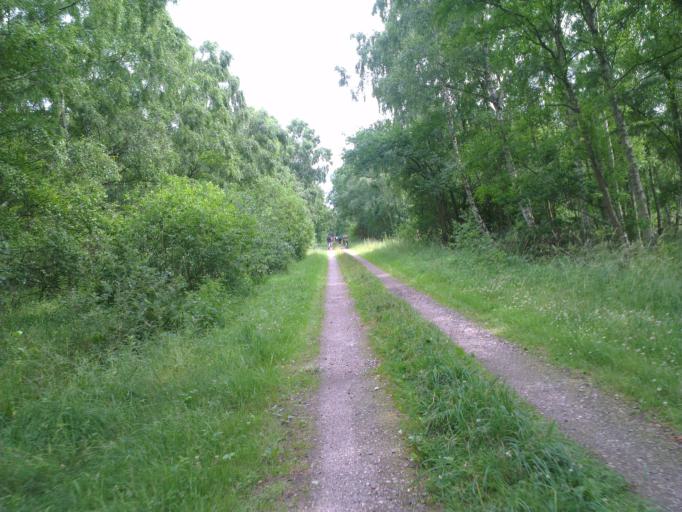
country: DK
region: Capital Region
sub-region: Frederikssund Kommune
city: Jaegerspris
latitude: 55.8909
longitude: 11.9414
